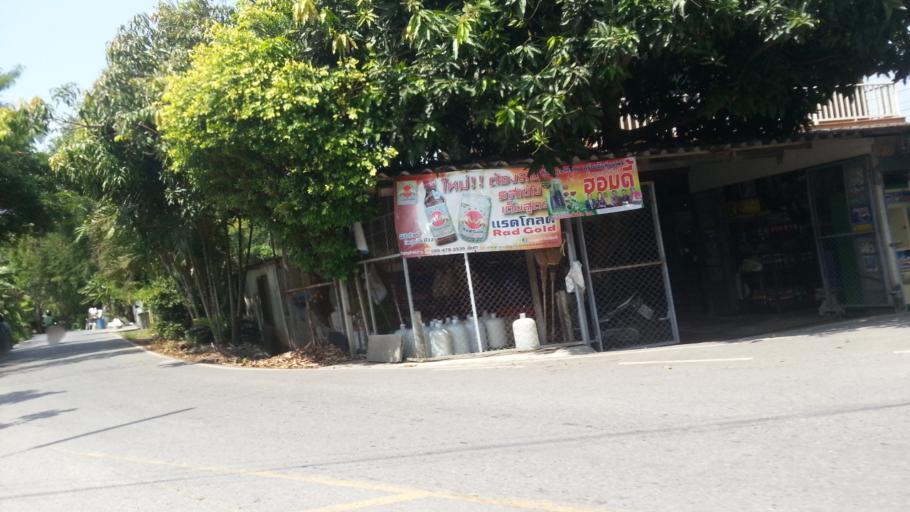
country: TH
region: Pathum Thani
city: Ban Rangsit
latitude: 14.0445
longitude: 100.8027
